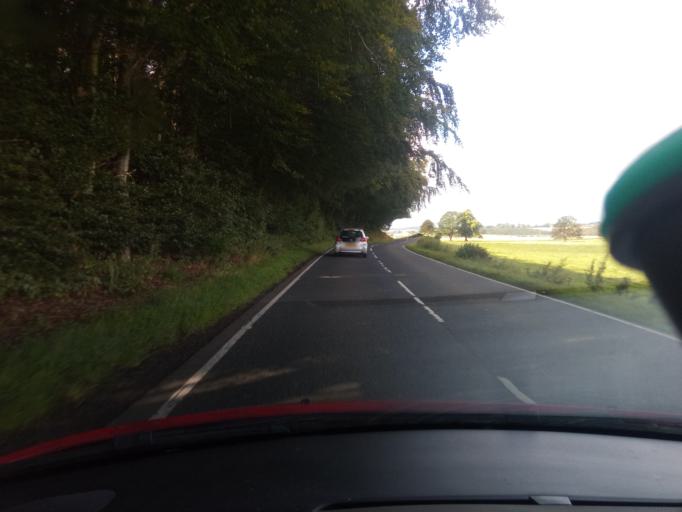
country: GB
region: Scotland
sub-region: The Scottish Borders
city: Jedburgh
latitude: 55.5729
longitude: -2.5466
